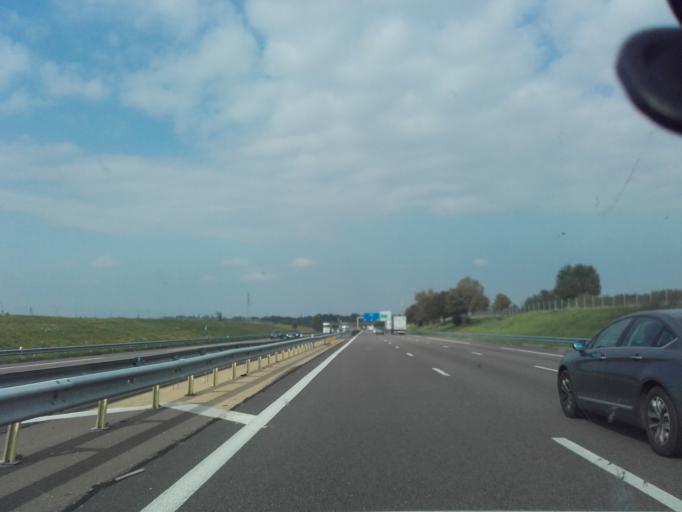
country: FR
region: Bourgogne
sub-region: Departement de Saone-et-Loire
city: Sevrey
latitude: 46.7441
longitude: 4.8335
